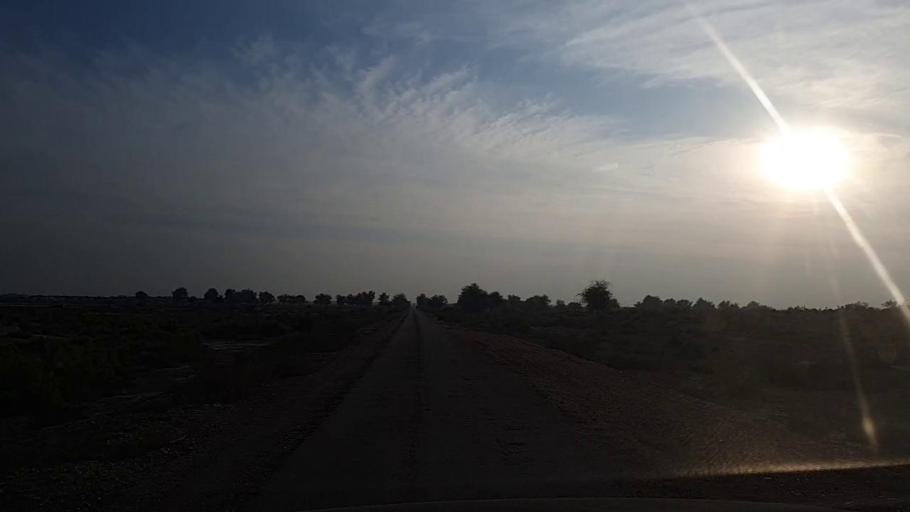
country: PK
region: Sindh
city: Jam Sahib
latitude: 26.4115
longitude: 68.5119
